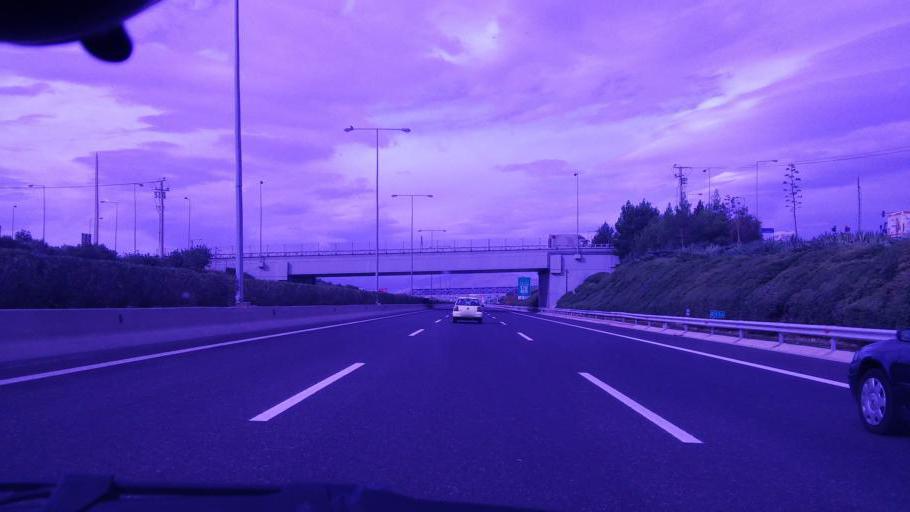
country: GR
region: Attica
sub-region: Nomarchia Dytikis Attikis
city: Aspropyrgos
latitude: 38.0897
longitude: 23.6223
